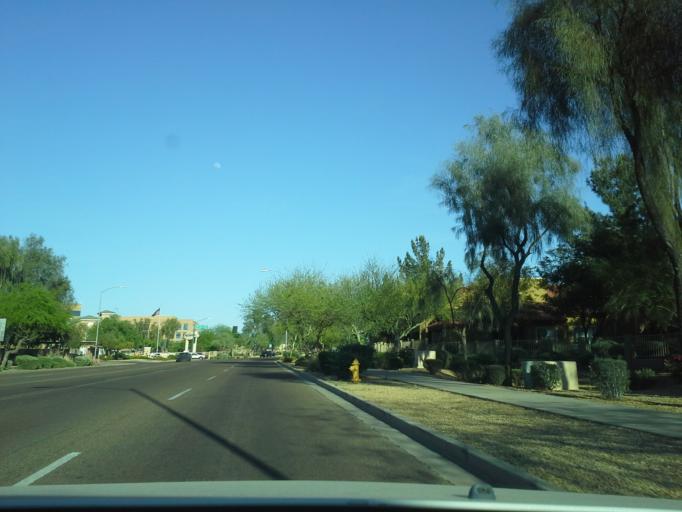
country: US
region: Arizona
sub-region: Maricopa County
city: Glendale
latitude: 33.6627
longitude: -112.1190
